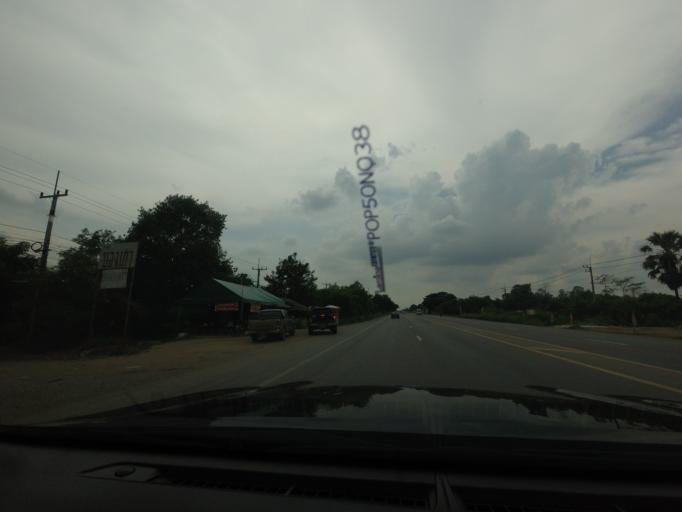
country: TH
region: Nakhon Pathom
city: Kamphaeng Saen
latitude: 14.0103
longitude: 99.9534
